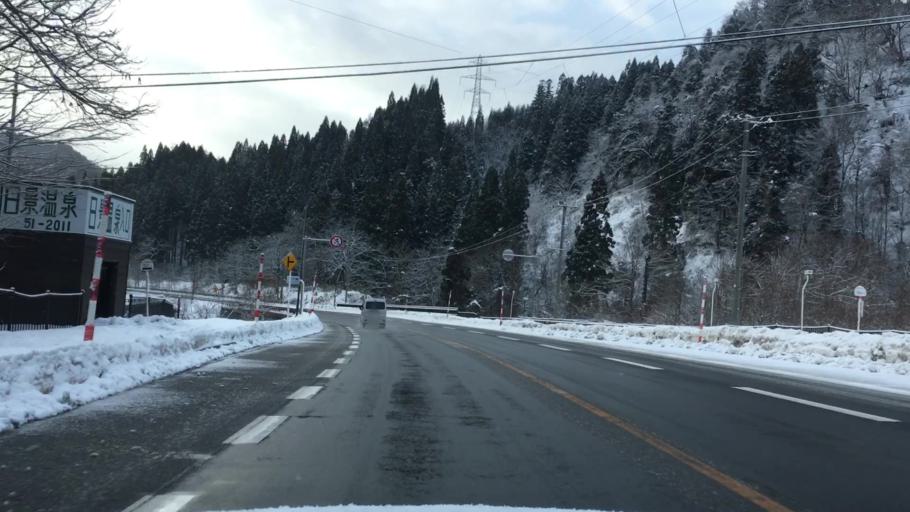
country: JP
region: Akita
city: Odate
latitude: 40.4154
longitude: 140.6115
